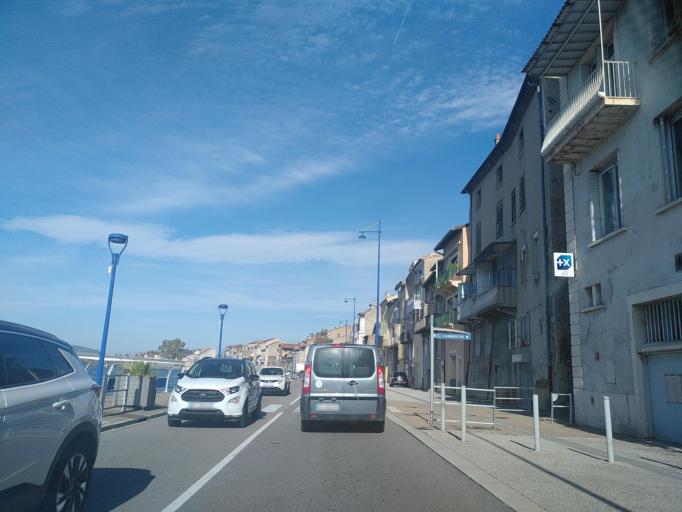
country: FR
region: Rhone-Alpes
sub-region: Departement de la Drome
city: Saint-Vallier
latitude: 45.1794
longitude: 4.8137
